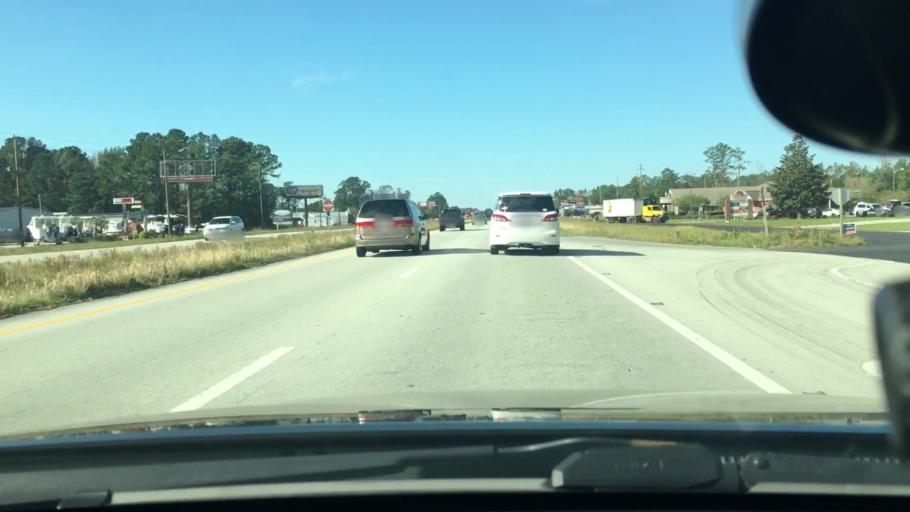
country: US
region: North Carolina
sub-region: Craven County
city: James City
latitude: 35.0604
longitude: -77.0199
